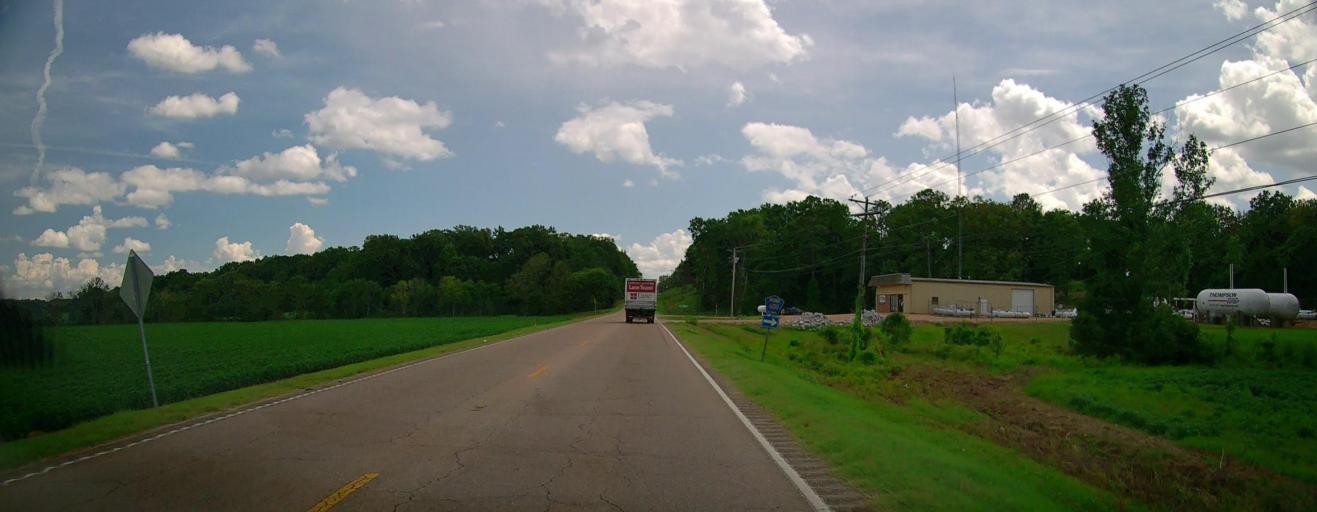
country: US
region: Mississippi
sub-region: Lee County
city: Shannon
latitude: 34.1354
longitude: -88.7194
